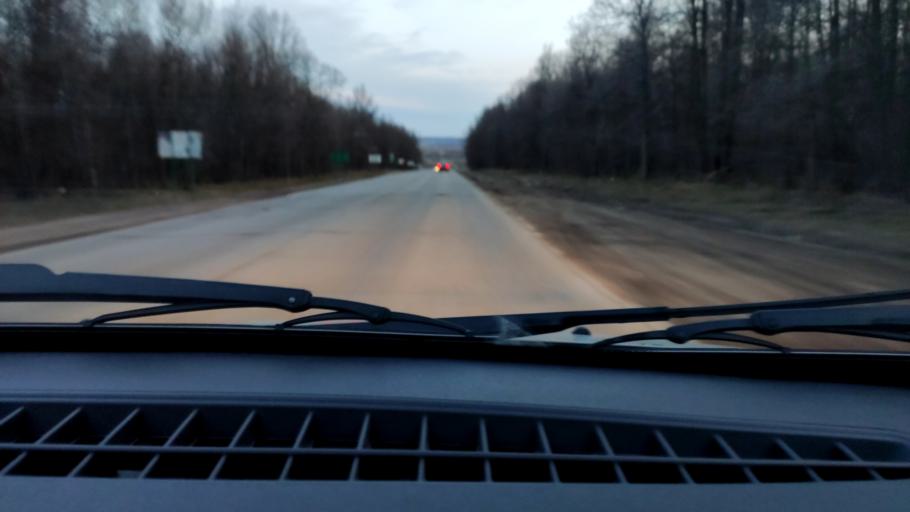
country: RU
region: Bashkortostan
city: Iglino
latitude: 54.7694
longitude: 56.4140
